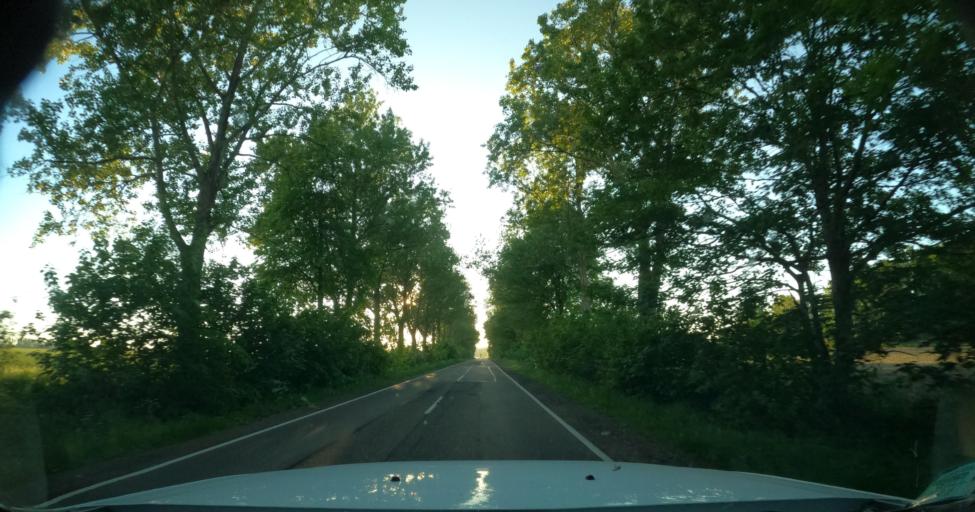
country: PL
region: Pomeranian Voivodeship
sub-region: Powiat slupski
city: Potegowo
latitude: 54.4155
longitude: 17.4105
